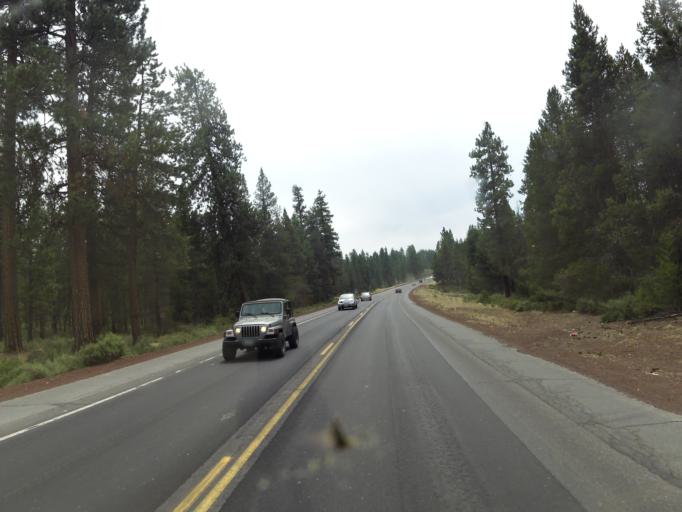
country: US
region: Oregon
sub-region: Deschutes County
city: Three Rivers
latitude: 43.8193
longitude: -121.4280
